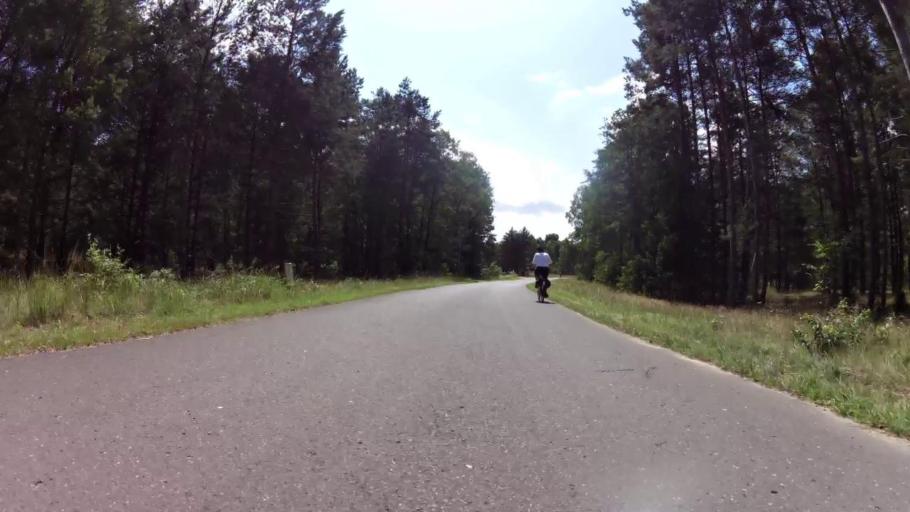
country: PL
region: West Pomeranian Voivodeship
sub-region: Powiat choszczenski
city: Drawno
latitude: 53.3789
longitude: 15.7290
